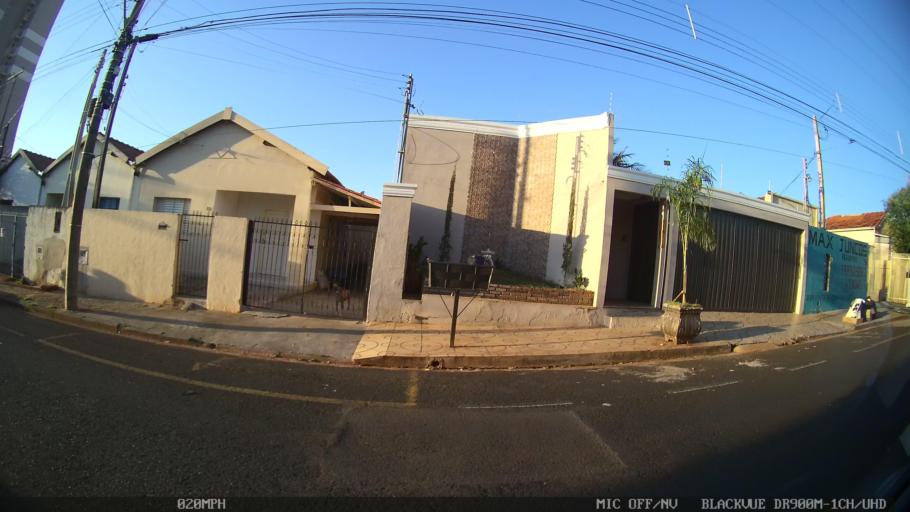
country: BR
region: Sao Paulo
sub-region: Sao Jose Do Rio Preto
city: Sao Jose do Rio Preto
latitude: -20.7972
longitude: -49.3729
